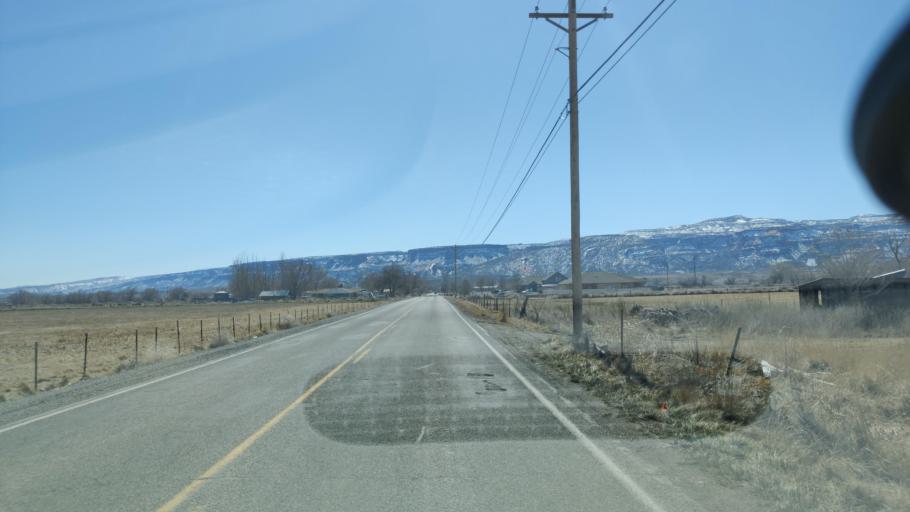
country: US
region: Colorado
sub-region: Mesa County
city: Fruita
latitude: 39.1477
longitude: -108.7011
